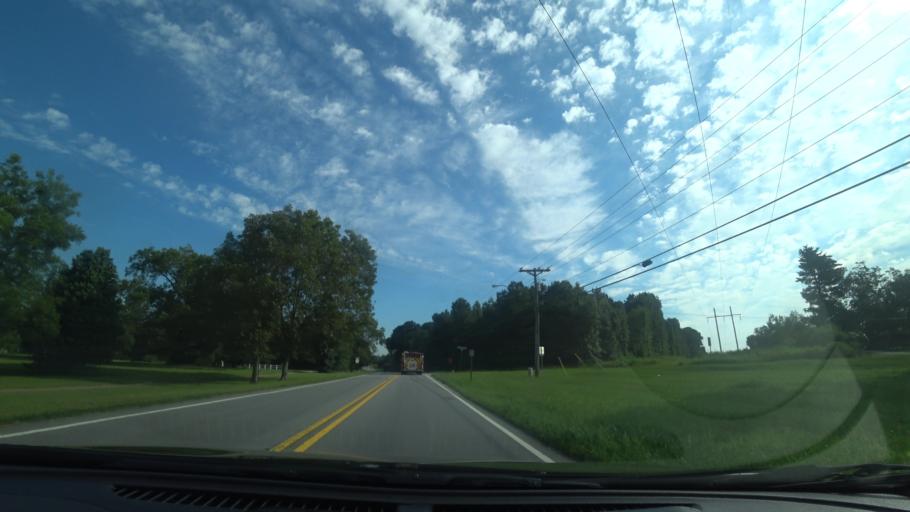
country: US
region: Georgia
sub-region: Gwinnett County
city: Grayson
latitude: 33.8403
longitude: -83.9592
